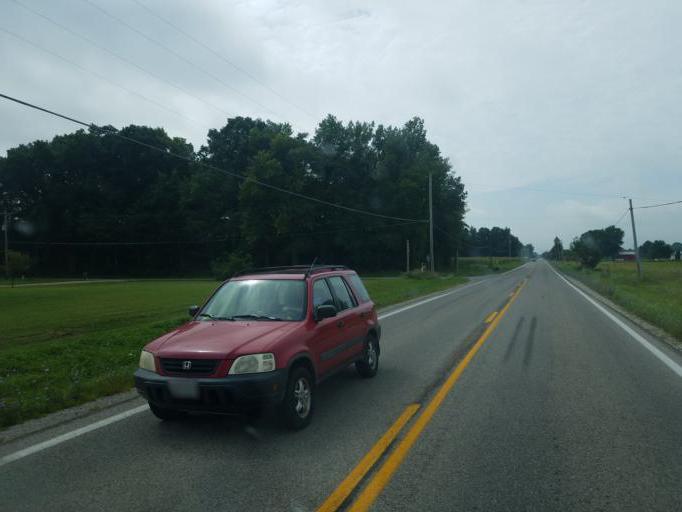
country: US
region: Ohio
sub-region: Morrow County
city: Cardington
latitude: 40.4126
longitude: -82.8259
